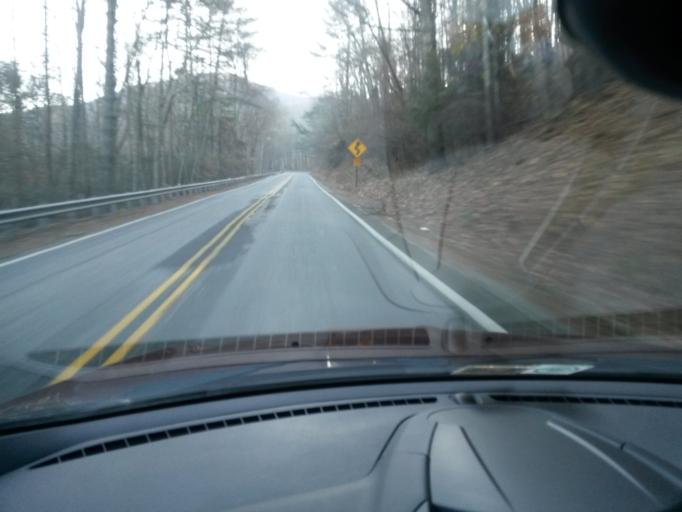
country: US
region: Virginia
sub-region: City of Buena Vista
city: Buena Vista
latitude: 37.7450
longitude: -79.2629
